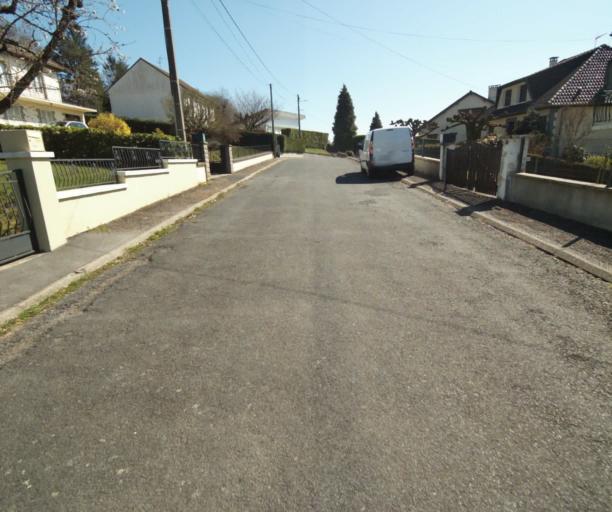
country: FR
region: Limousin
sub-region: Departement de la Correze
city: Saint-Mexant
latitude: 45.2800
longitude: 1.6623
